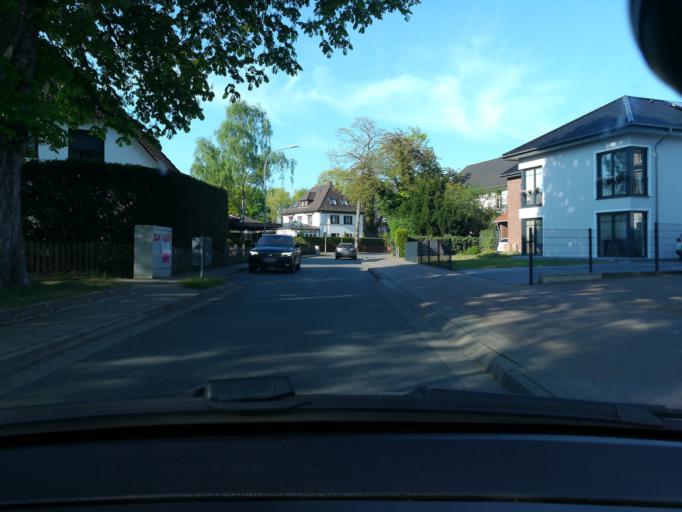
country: DE
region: North Rhine-Westphalia
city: Versmold
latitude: 52.0378
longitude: 8.1515
